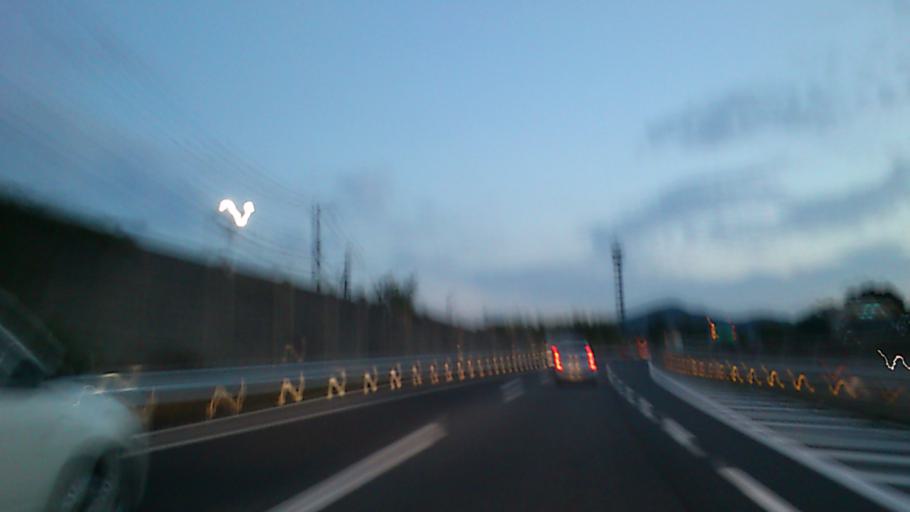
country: JP
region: Gifu
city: Tajimi
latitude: 35.3449
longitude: 137.1009
